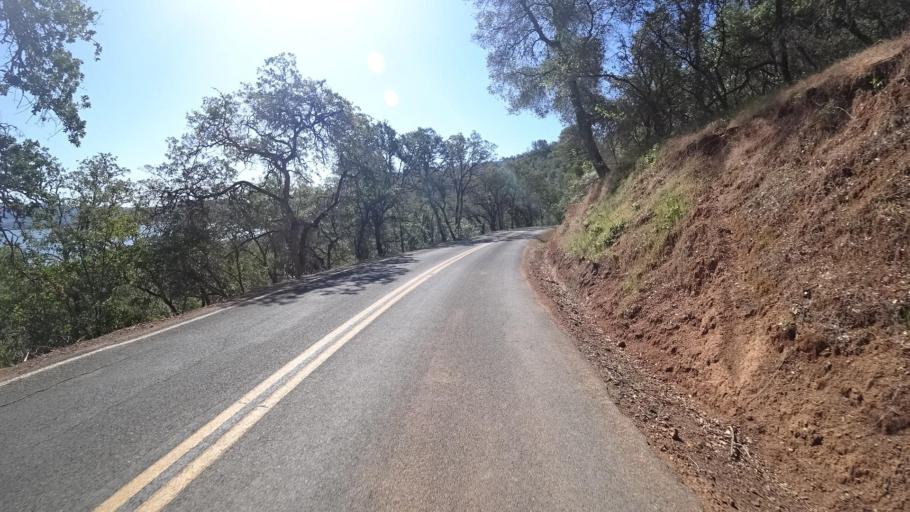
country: US
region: California
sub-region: Lake County
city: Clearlake Oaks
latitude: 38.9998
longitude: -122.7016
